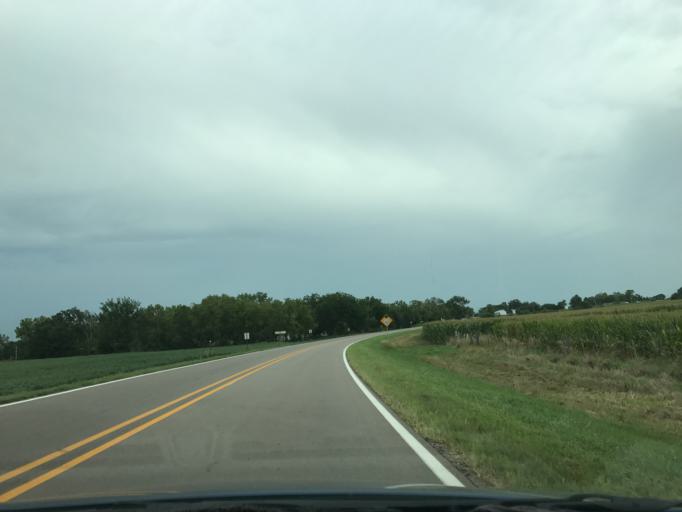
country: US
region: Nebraska
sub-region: Gage County
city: Beatrice
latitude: 40.2731
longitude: -96.7757
